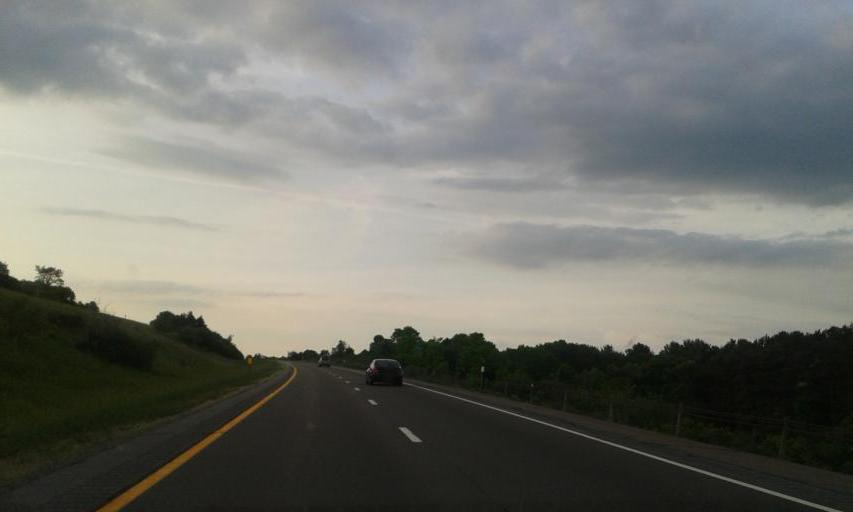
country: US
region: New York
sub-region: Broome County
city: Chenango Bridge
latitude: 42.2573
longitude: -75.9181
